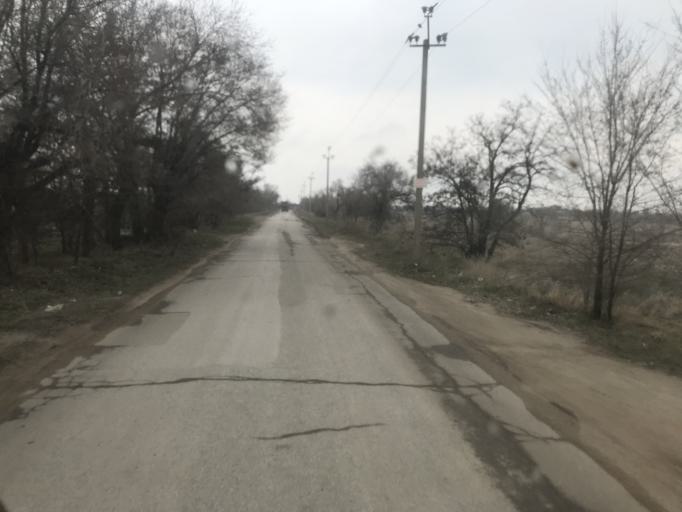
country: RU
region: Volgograd
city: Krasnoslobodsk
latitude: 48.5315
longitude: 44.6079
